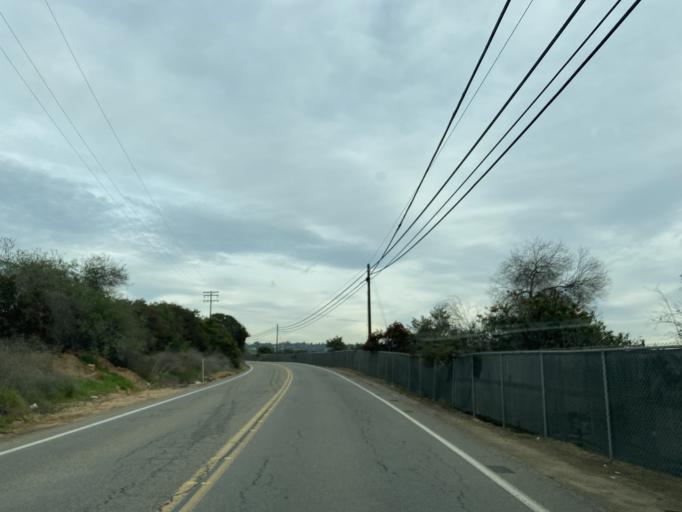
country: US
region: California
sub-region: San Diego County
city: Bonsall
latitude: 33.2597
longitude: -117.2621
